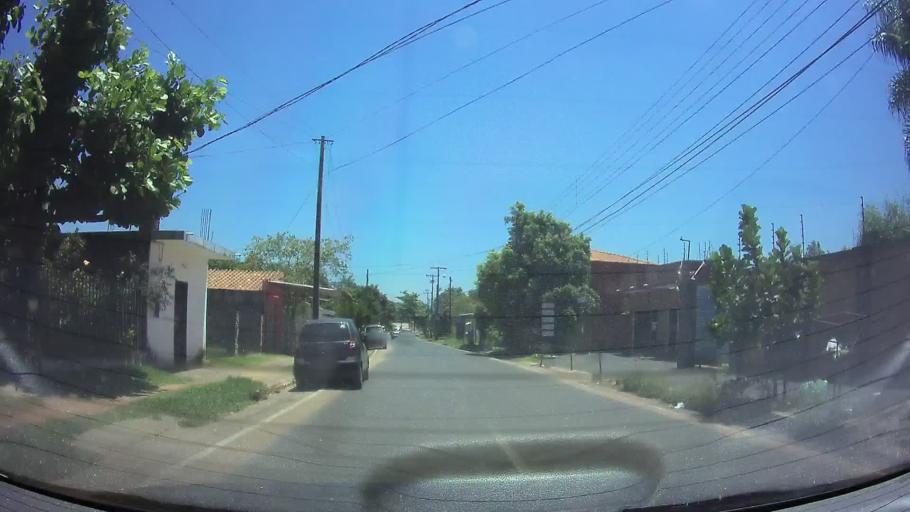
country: PY
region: Central
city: San Lorenzo
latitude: -25.2701
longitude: -57.5069
